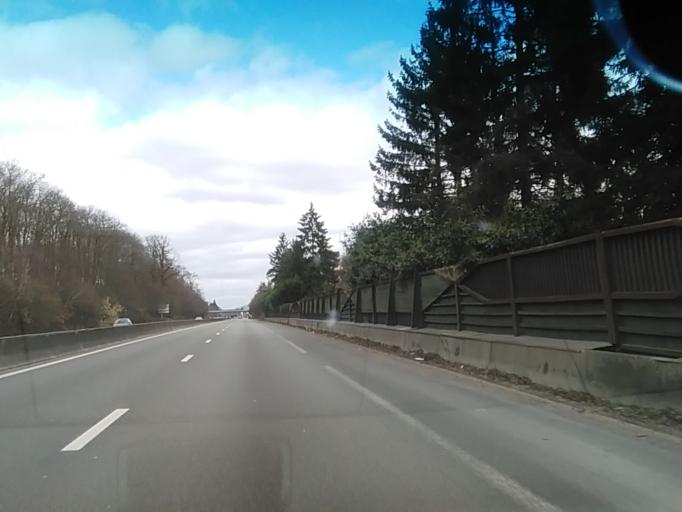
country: FR
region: Haute-Normandie
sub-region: Departement de la Seine-Maritime
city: Grand-Couronne
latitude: 49.3488
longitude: 1.0209
